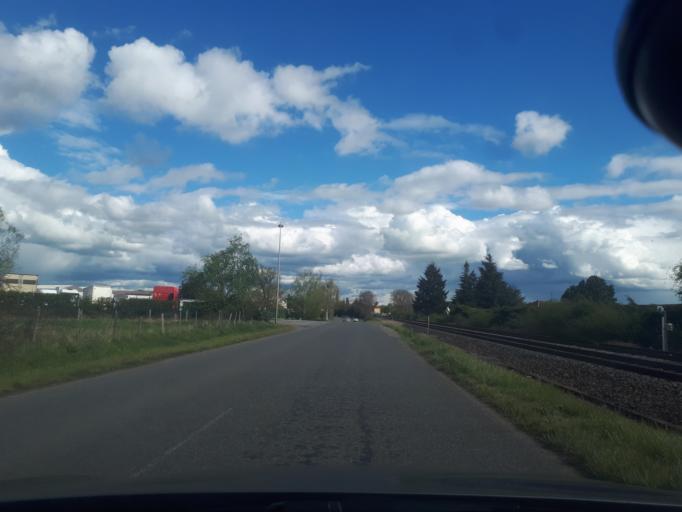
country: FR
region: Rhone-Alpes
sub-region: Departement de la Loire
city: Balbigny
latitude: 45.8228
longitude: 4.1811
